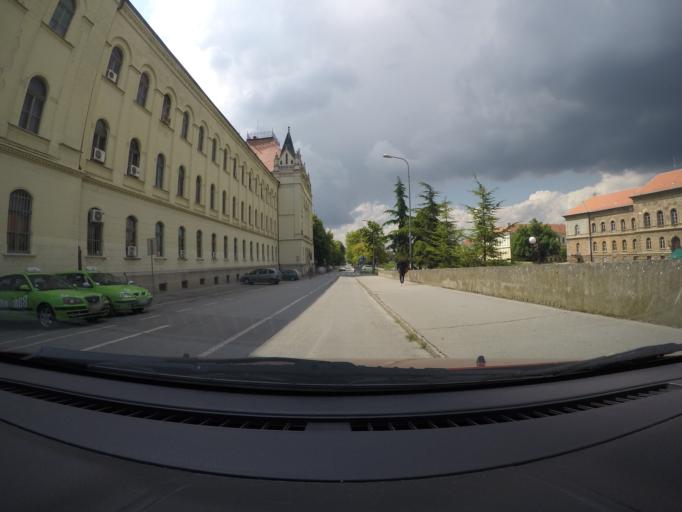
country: RS
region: Autonomna Pokrajina Vojvodina
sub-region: Srednjebanatski Okrug
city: Zrenjanin
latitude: 45.3789
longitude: 20.3891
